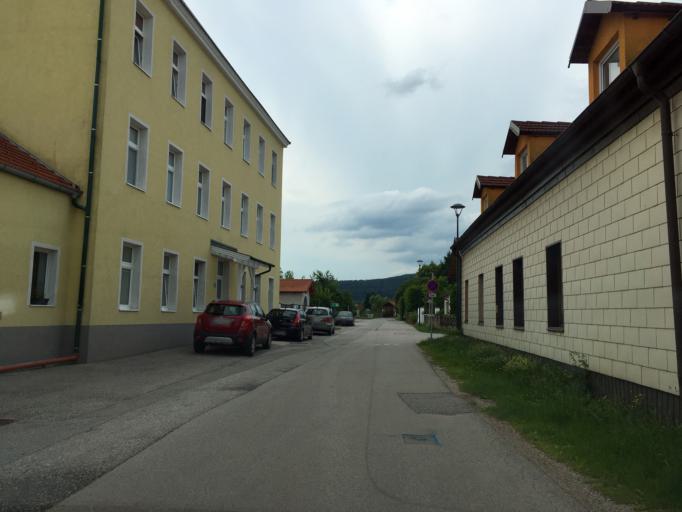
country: AT
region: Lower Austria
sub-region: Politischer Bezirk Wiener Neustadt
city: Bad Erlach
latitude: 47.7296
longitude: 16.2172
